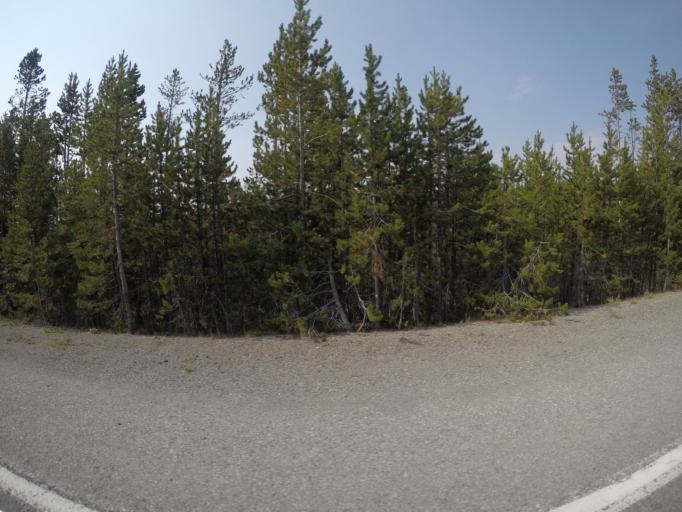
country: US
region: Montana
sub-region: Gallatin County
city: West Yellowstone
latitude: 44.7200
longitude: -110.6455
